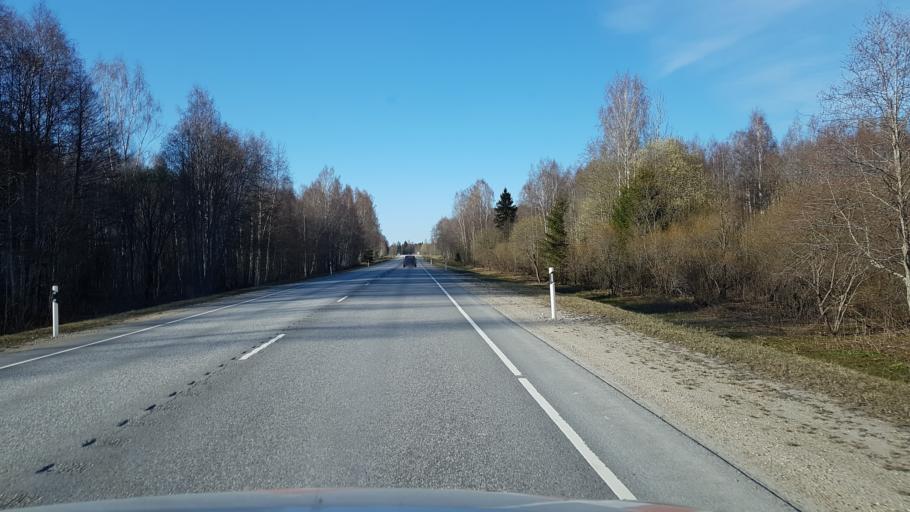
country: EE
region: Ida-Virumaa
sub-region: Johvi vald
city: Johvi
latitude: 59.1935
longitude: 27.3465
